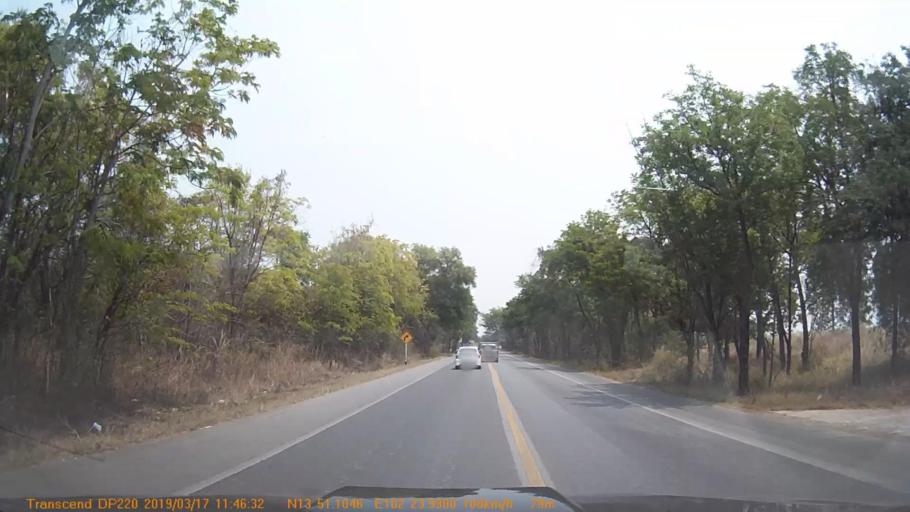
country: TH
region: Sa Kaeo
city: Watthana Nakhon
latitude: 13.8519
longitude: 102.4002
